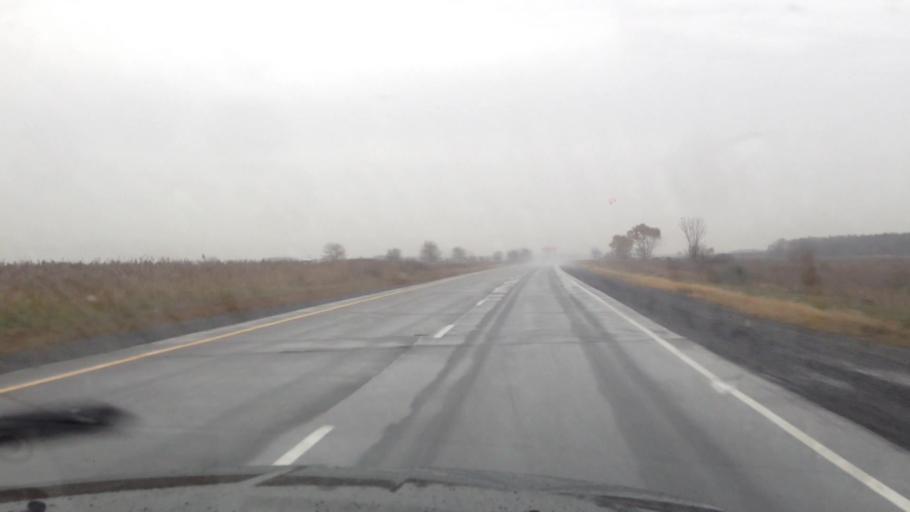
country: CA
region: Ontario
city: Casselman
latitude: 45.3298
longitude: -74.9552
